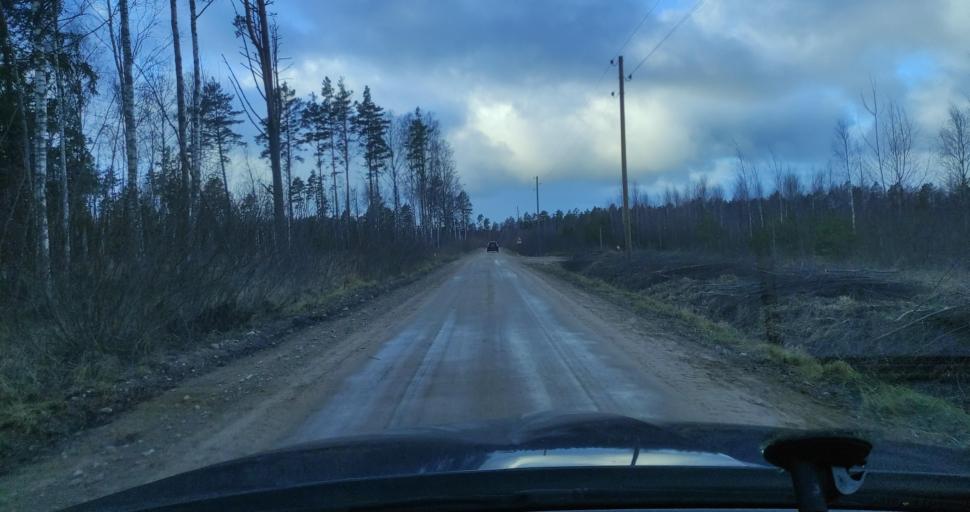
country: LV
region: Pavilostas
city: Pavilosta
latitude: 56.8583
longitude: 21.1685
